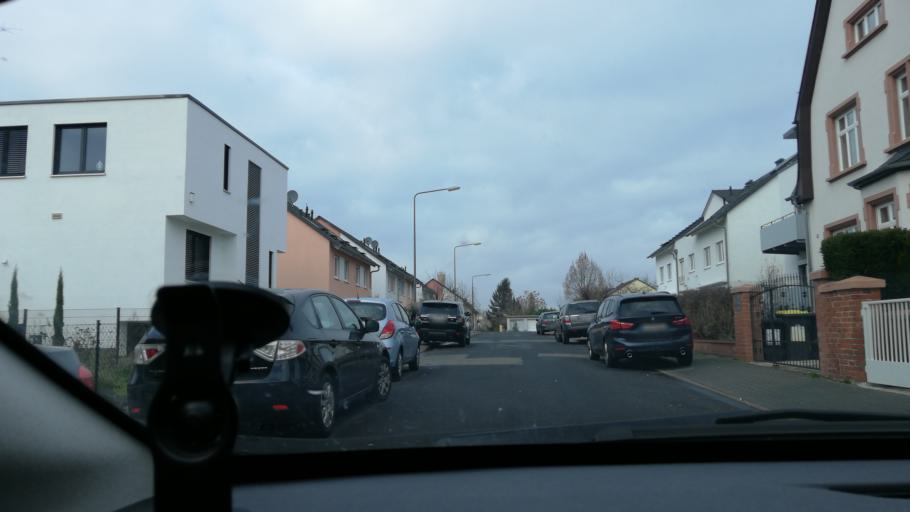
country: DE
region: Hesse
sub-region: Regierungsbezirk Darmstadt
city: Frankfurt am Main
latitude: 50.1465
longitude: 8.6955
